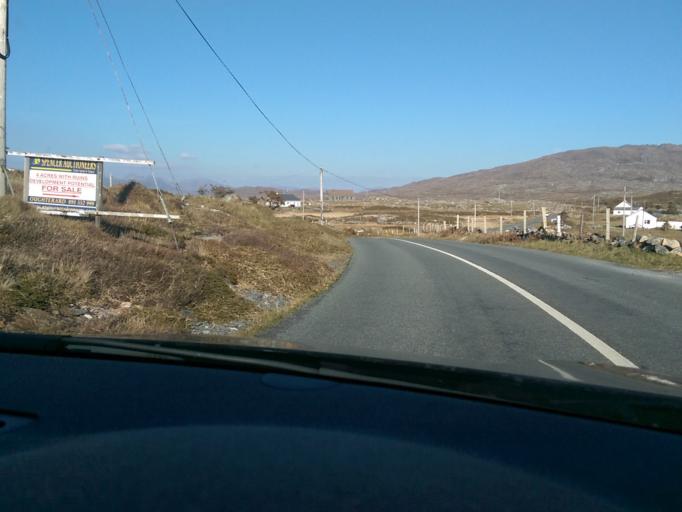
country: IE
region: Connaught
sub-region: County Galway
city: Clifden
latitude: 53.3952
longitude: -10.0116
